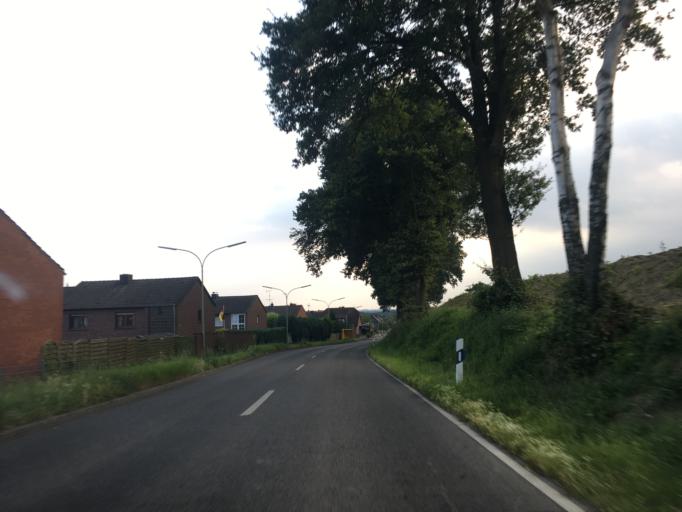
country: DE
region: North Rhine-Westphalia
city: Huckelhoven
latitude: 51.0721
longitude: 6.1998
